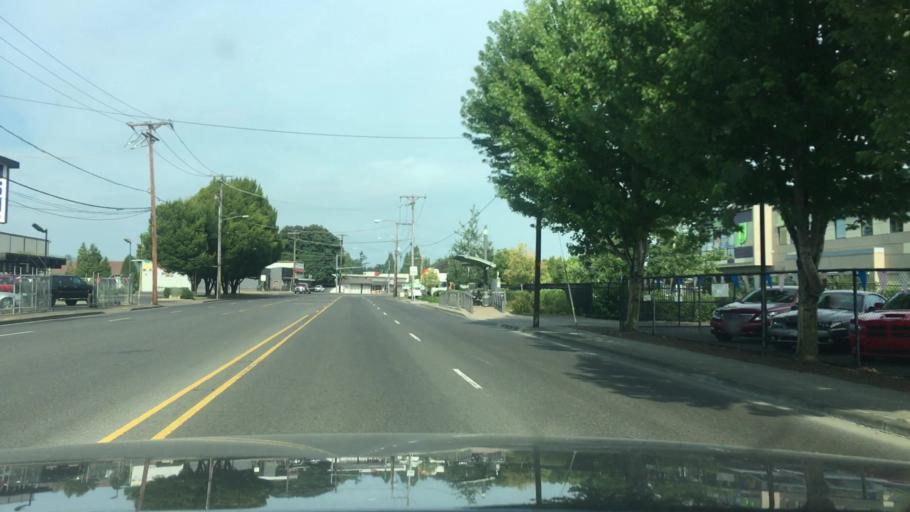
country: US
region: Oregon
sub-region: Lane County
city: Springfield
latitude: 44.0453
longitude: -123.0416
